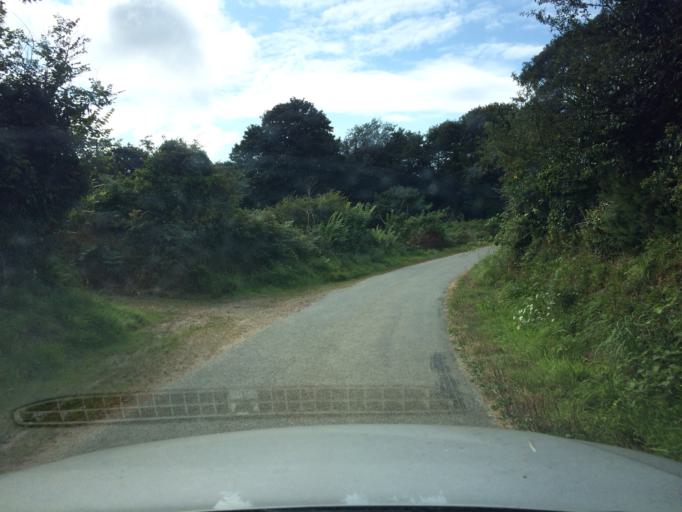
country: FR
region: Lower Normandy
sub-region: Departement de la Manche
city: Beaumont-Hague
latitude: 49.6873
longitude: -1.8861
